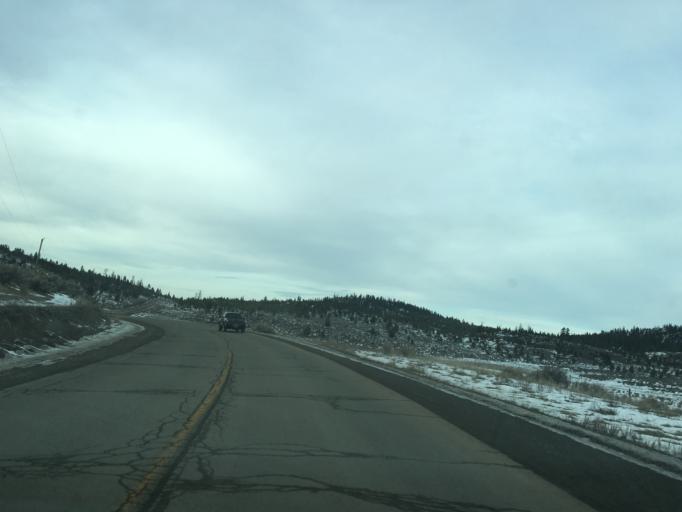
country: CA
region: British Columbia
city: Kamloops
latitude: 50.6288
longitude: -120.4414
